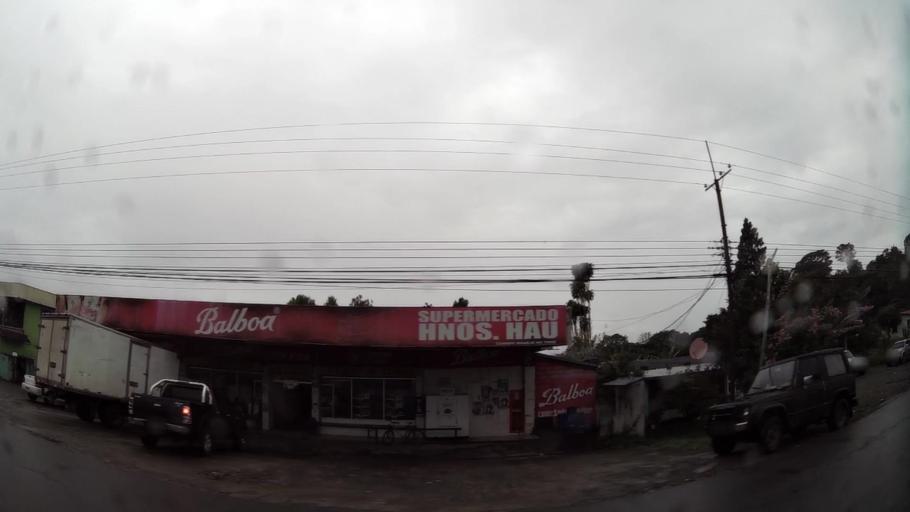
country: PA
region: Chiriqui
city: Volcan
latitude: 8.7726
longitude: -82.6369
